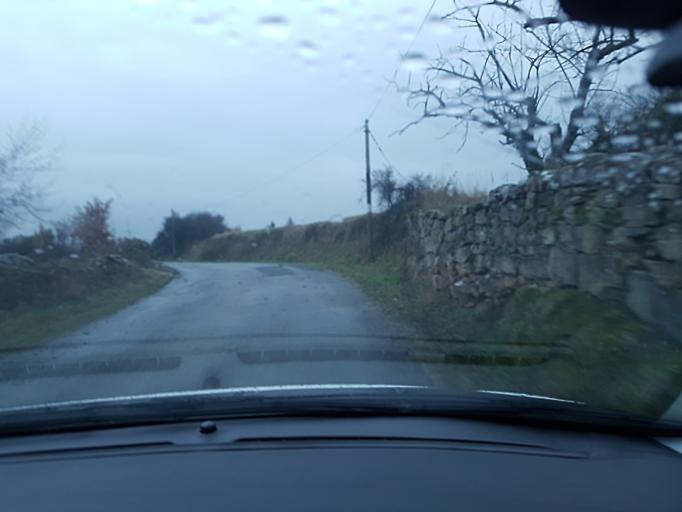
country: FR
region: Rhone-Alpes
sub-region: Departement du Rhone
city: Mornant
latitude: 45.6159
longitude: 4.6873
